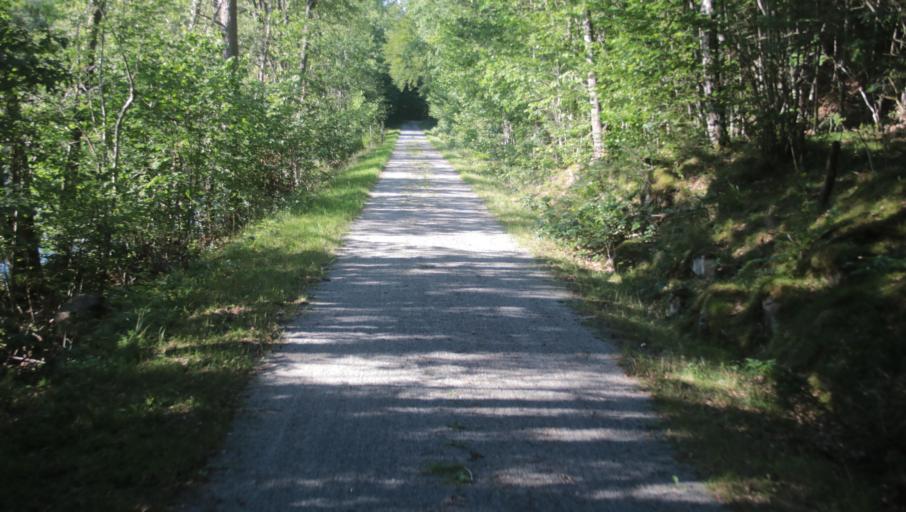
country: SE
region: Blekinge
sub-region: Karlshamns Kommun
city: Svangsta
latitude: 56.3388
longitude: 14.6969
